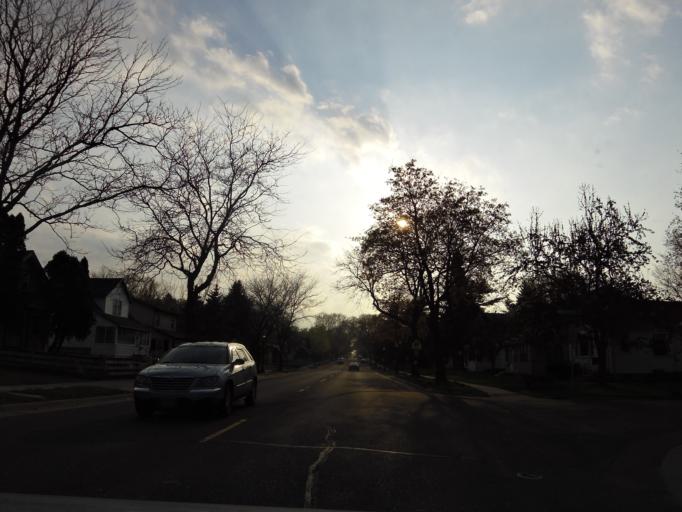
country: US
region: Minnesota
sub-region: Ramsey County
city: Maplewood
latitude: 44.9631
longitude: -93.0191
